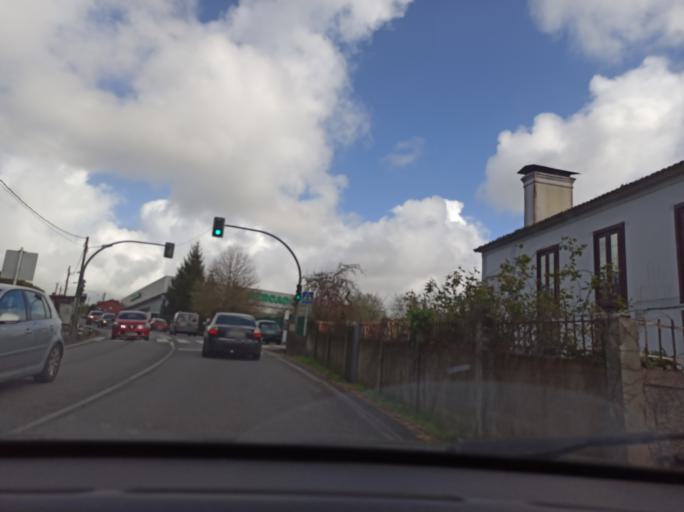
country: ES
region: Galicia
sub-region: Provincia da Coruna
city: Oleiros
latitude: 43.3329
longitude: -8.3075
